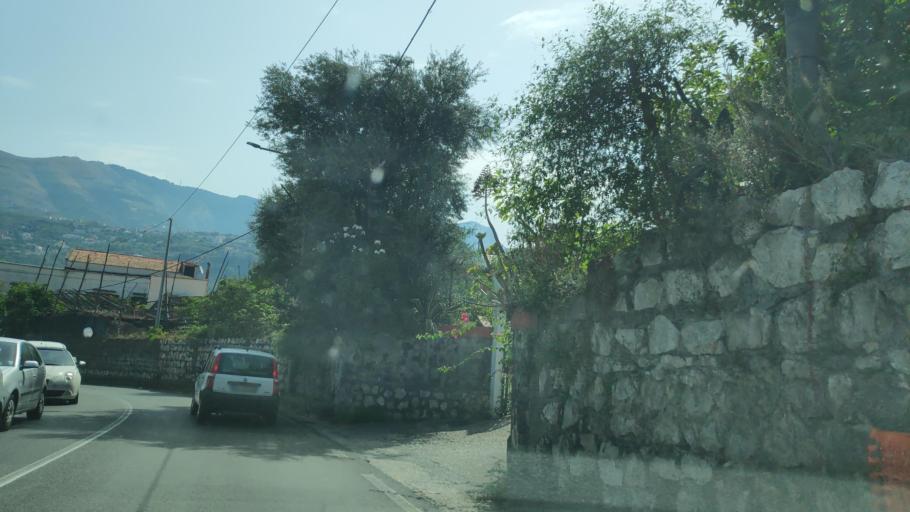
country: IT
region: Campania
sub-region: Provincia di Napoli
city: Vico Equense
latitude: 40.6557
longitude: 14.4215
